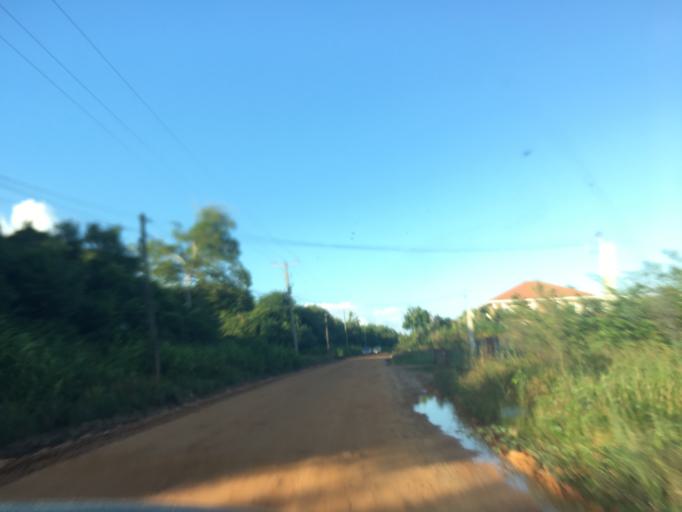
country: BZ
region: Stann Creek
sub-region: Dangriga
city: Dangriga
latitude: 16.8306
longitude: -88.2669
